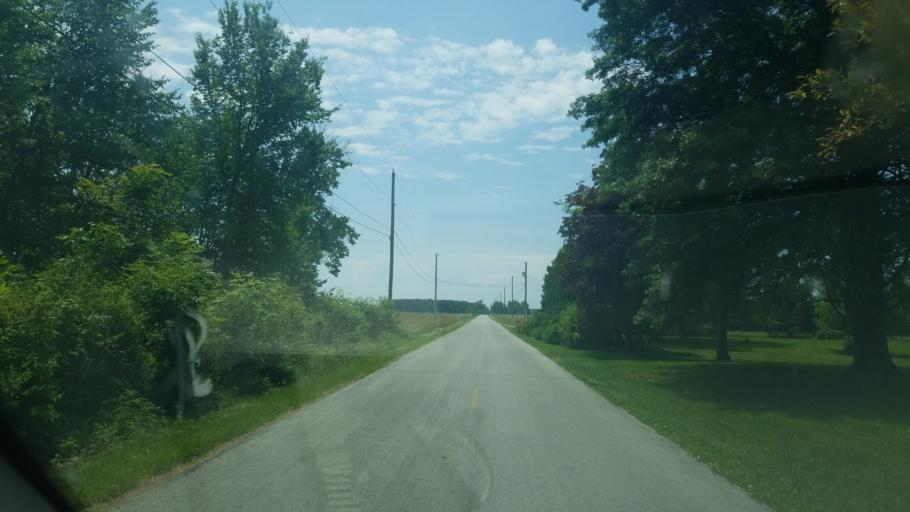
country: US
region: Ohio
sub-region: Wood County
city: North Baltimore
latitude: 41.2297
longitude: -83.6211
